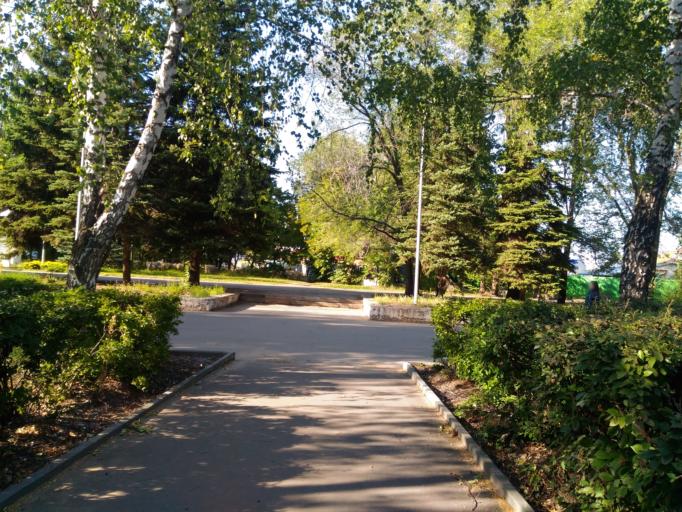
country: RU
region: Ulyanovsk
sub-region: Ulyanovskiy Rayon
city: Ulyanovsk
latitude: 54.3534
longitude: 48.5419
